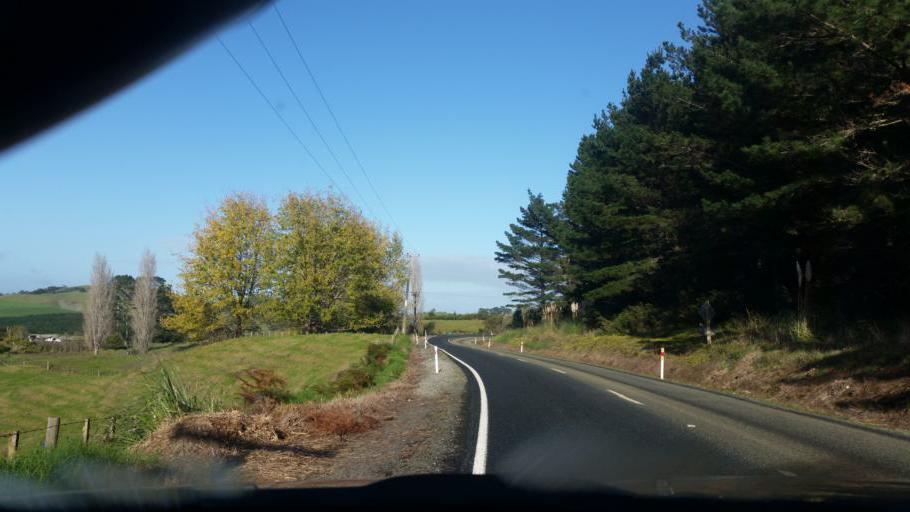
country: NZ
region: Auckland
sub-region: Auckland
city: Wellsford
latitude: -36.2288
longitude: 174.4465
